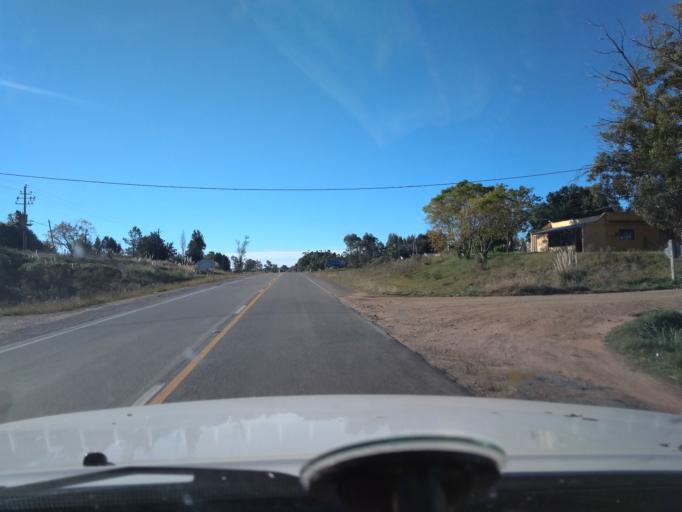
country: UY
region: Canelones
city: Sauce
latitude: -34.6121
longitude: -56.0488
